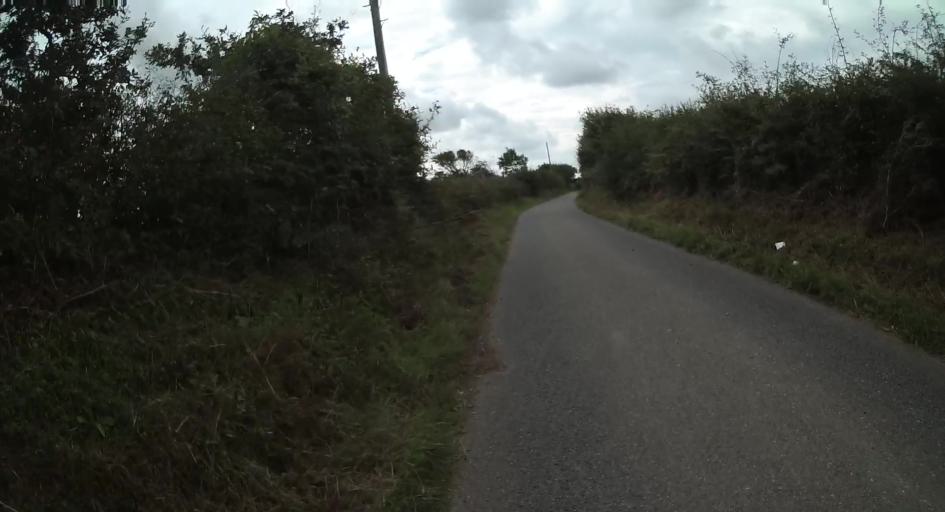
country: GB
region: England
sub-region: Isle of Wight
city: Niton
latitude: 50.6449
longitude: -1.2743
